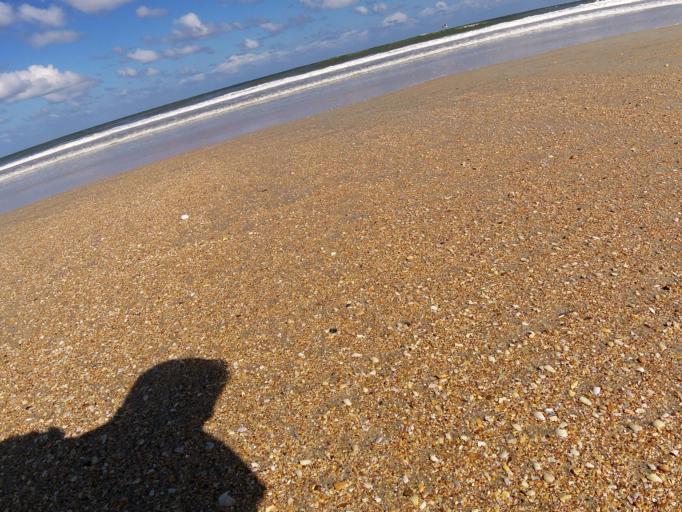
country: US
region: Florida
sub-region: Saint Johns County
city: Palm Valley
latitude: 30.0801
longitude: -81.3356
